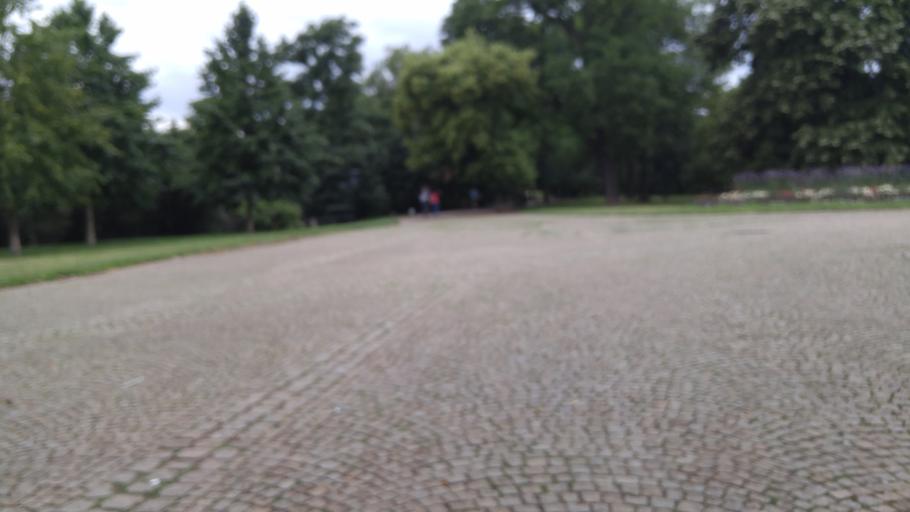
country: CZ
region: Praha
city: Prague
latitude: 50.0960
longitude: 14.4251
